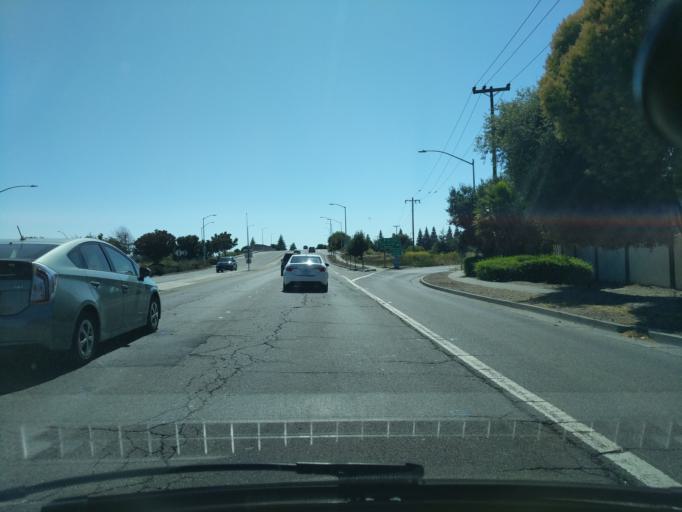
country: US
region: California
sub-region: Alameda County
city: Hayward
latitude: 37.6575
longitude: -122.0991
